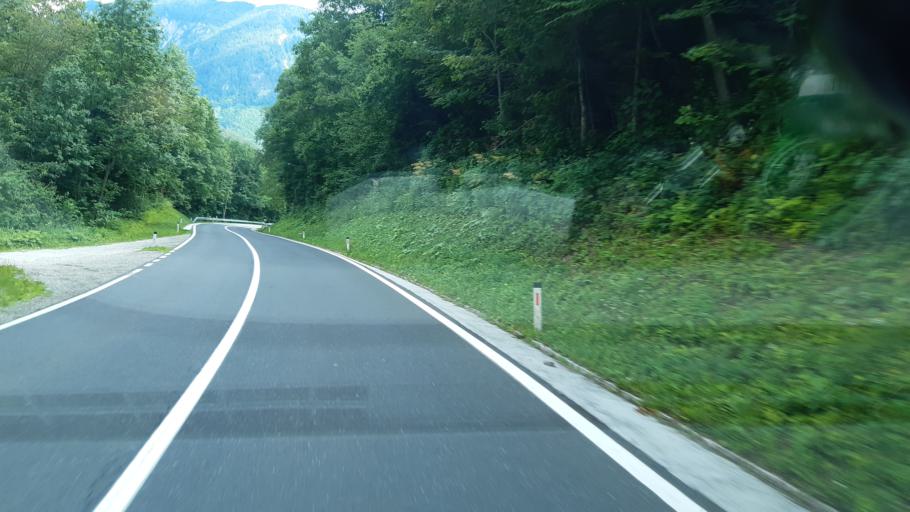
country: SI
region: Trzic
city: Trzic
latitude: 46.3768
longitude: 14.2970
